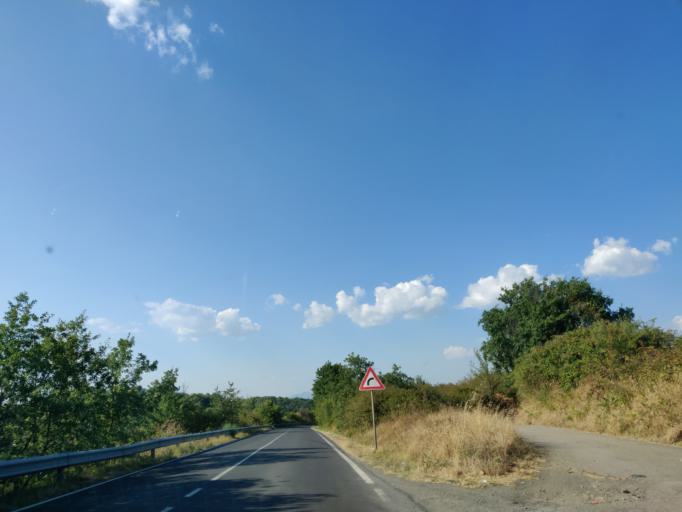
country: IT
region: Latium
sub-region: Provincia di Viterbo
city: Latera
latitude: 42.6419
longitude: 11.8385
